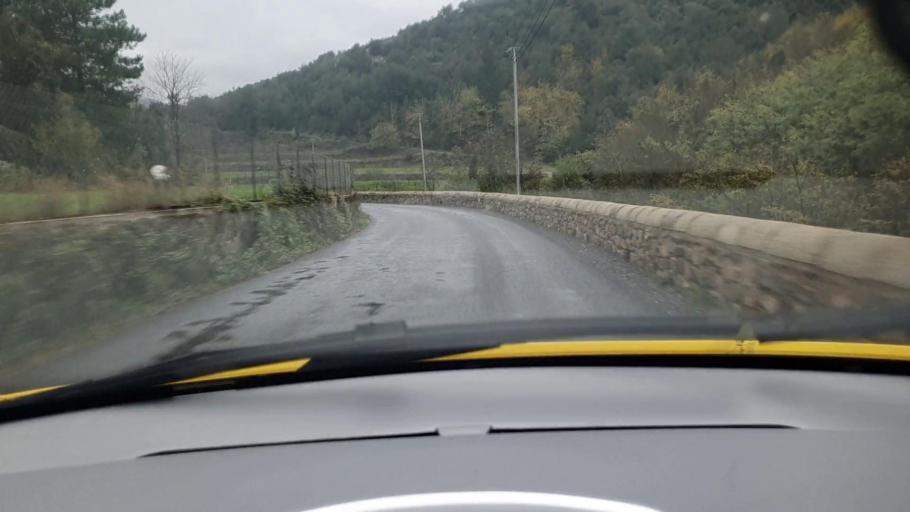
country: FR
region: Languedoc-Roussillon
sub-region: Departement du Gard
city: Sumene
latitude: 43.9911
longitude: 3.7133
